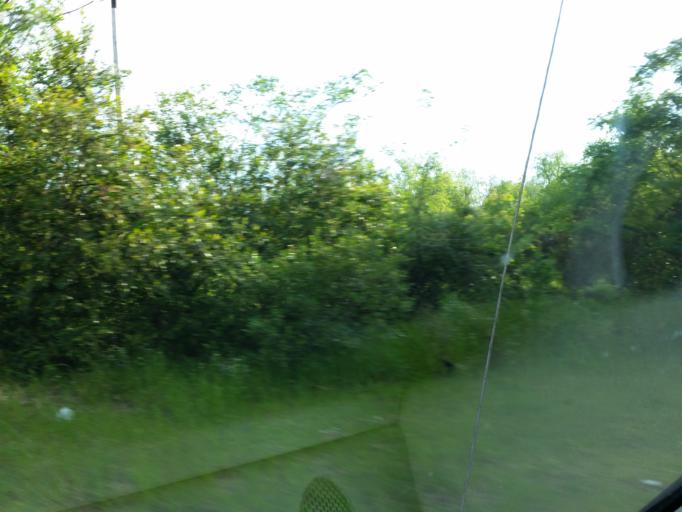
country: US
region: Georgia
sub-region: Crisp County
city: Cordele
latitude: 31.9784
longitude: -83.7886
